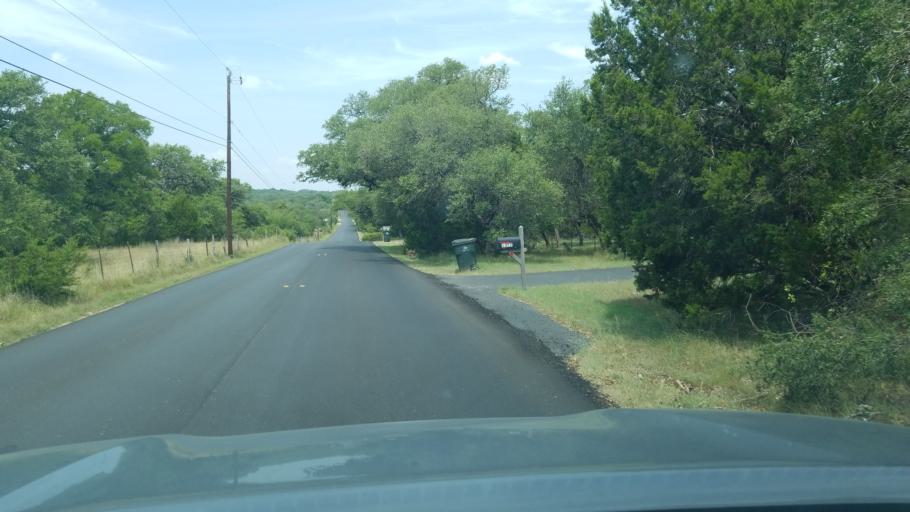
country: US
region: Texas
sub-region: Comal County
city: Bulverde
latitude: 29.7597
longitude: -98.4729
